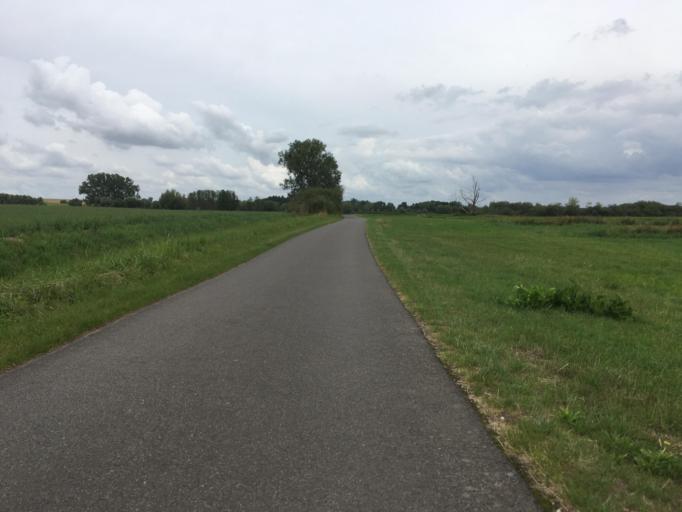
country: DE
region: Brandenburg
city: Prenzlau
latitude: 53.2696
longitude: 13.8475
